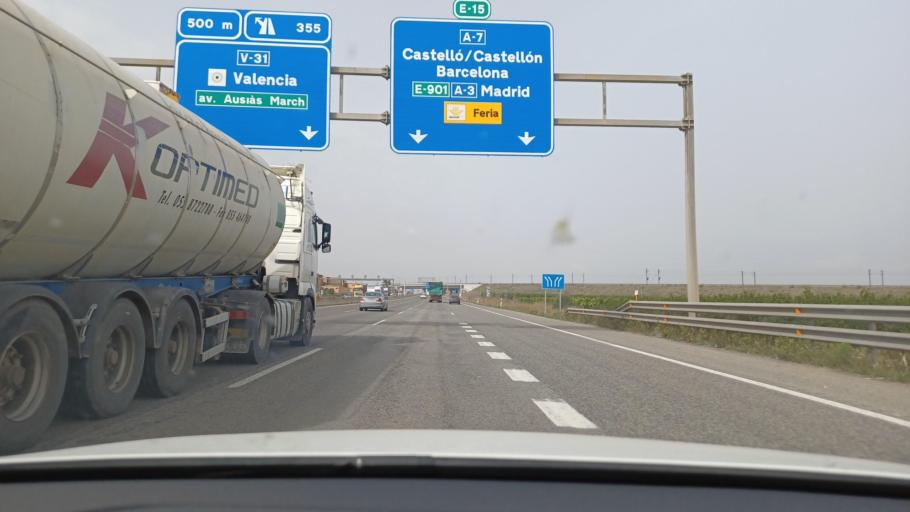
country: ES
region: Valencia
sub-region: Provincia de Valencia
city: Silla
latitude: 39.3363
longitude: -0.4311
